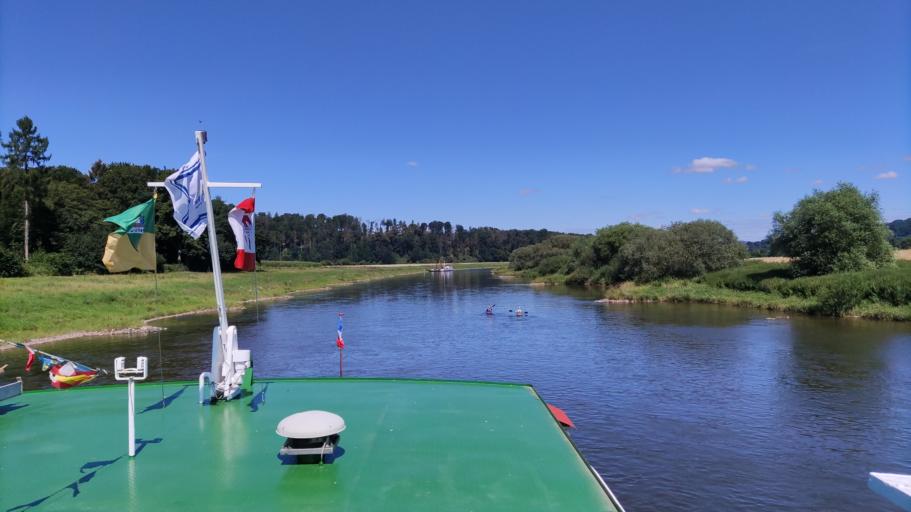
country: DE
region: Lower Saxony
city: Furstenberg
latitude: 51.7140
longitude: 9.3902
